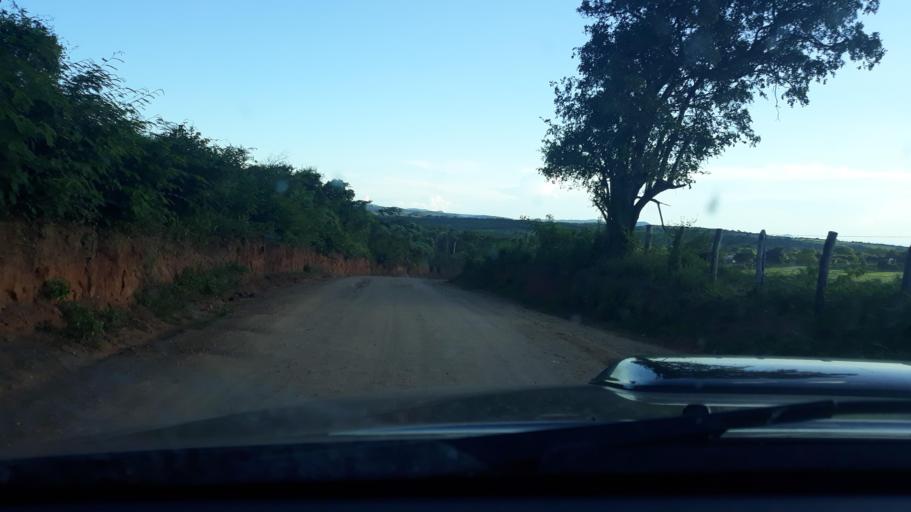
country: BR
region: Bahia
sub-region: Riacho De Santana
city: Riacho de Santana
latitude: -13.8194
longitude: -42.7240
